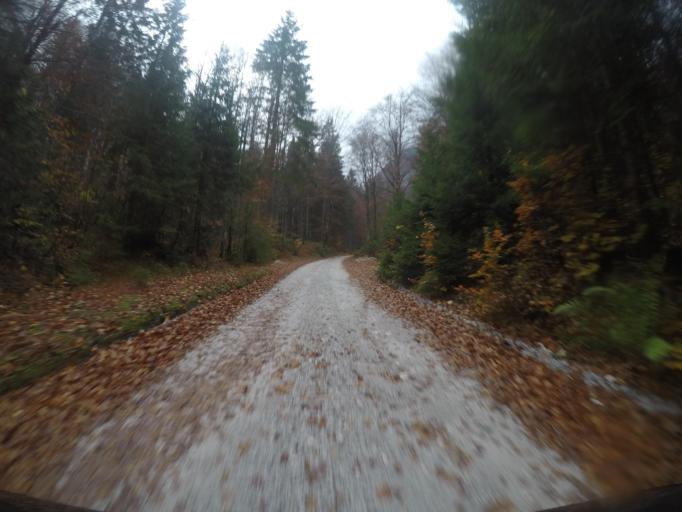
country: SI
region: Kranjska Gora
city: Mojstrana
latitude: 46.4155
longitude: 13.8514
